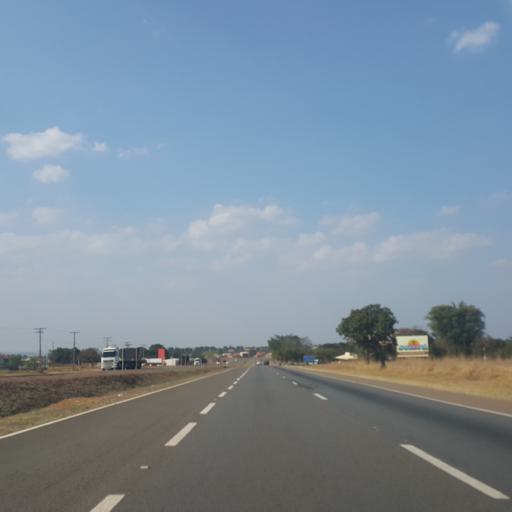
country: BR
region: Goias
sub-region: Abadiania
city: Abadiania
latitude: -16.1934
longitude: -48.7277
